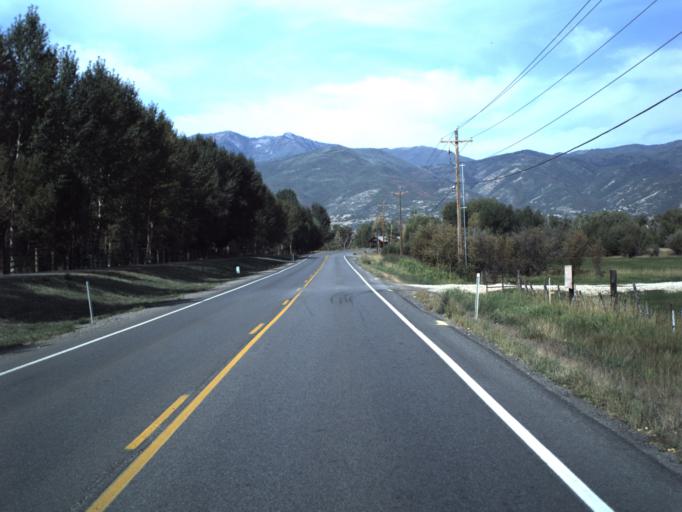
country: US
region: Utah
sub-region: Wasatch County
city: Midway
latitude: 40.5070
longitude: -111.4452
